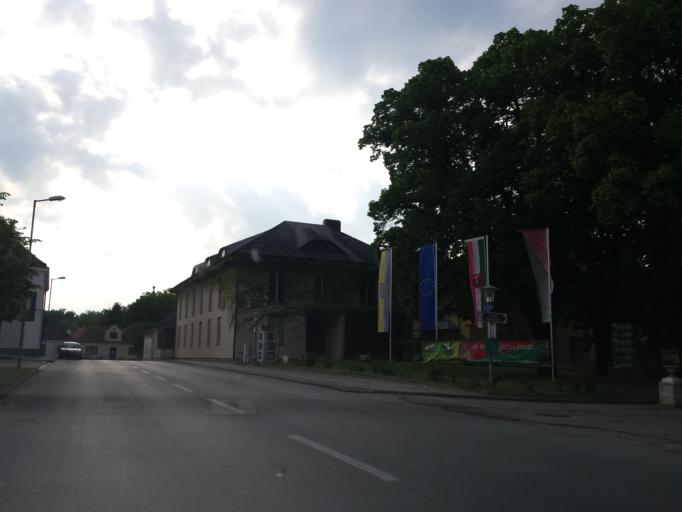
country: AT
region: Lower Austria
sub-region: Politischer Bezirk Ganserndorf
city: Marchegg
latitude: 48.2801
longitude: 16.9076
